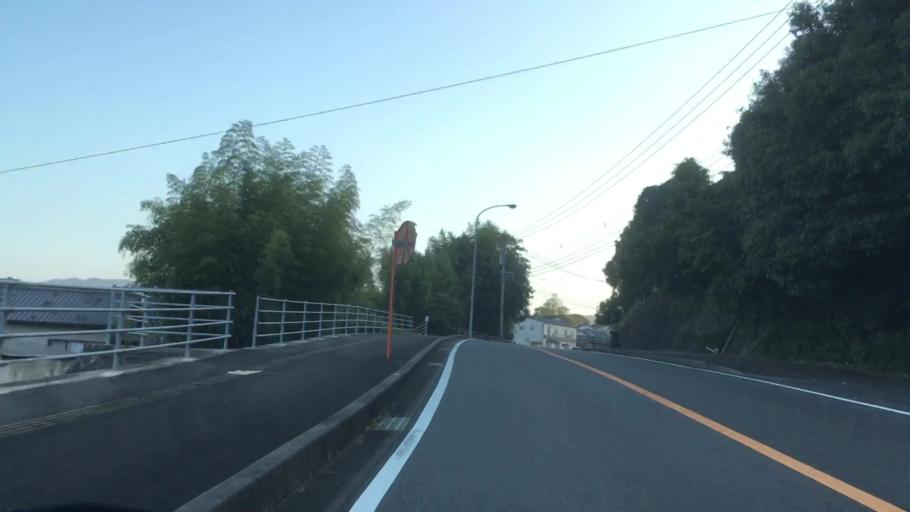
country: JP
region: Nagasaki
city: Sasebo
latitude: 33.0068
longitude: 129.7312
